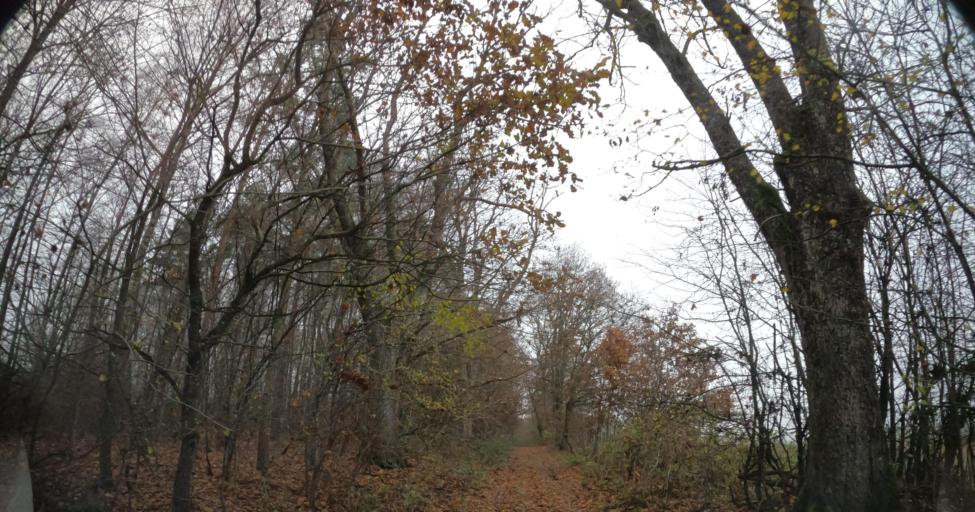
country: PL
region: West Pomeranian Voivodeship
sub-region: Powiat drawski
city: Drawsko Pomorskie
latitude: 53.5964
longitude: 15.7771
